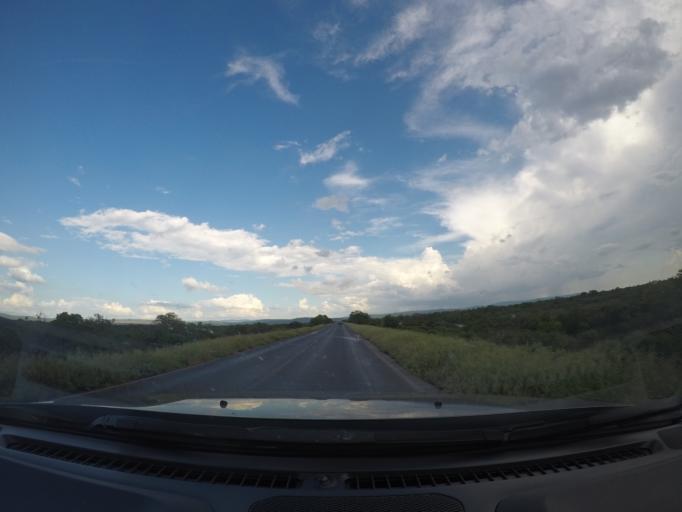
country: BR
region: Bahia
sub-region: Ibotirama
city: Ibotirama
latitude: -12.1653
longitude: -43.2790
